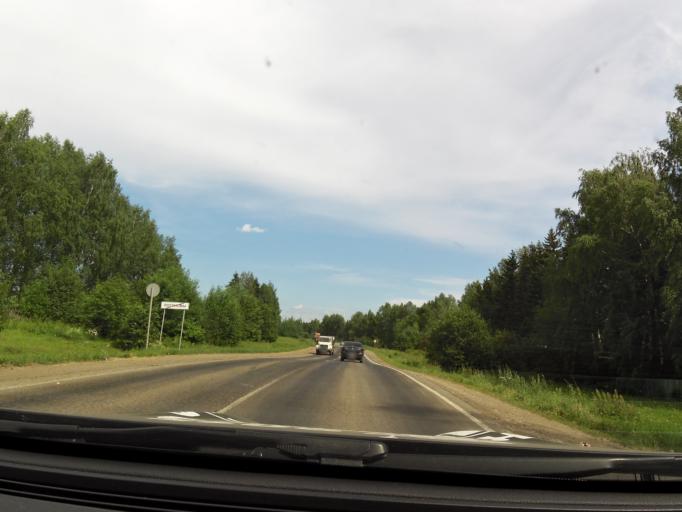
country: RU
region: Kirov
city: Vakhrushi
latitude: 58.6775
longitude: 49.9801
